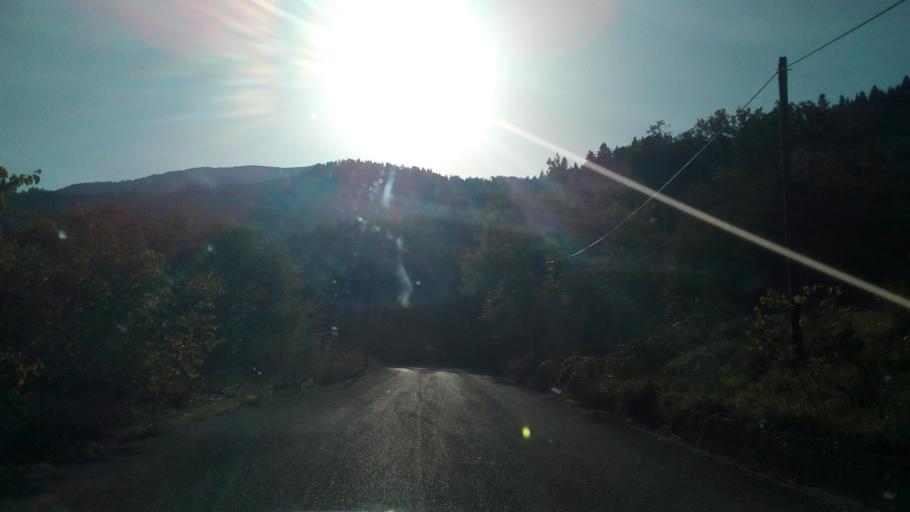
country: GR
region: West Greece
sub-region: Nomos Aitolias kai Akarnanias
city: Thermo
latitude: 38.6552
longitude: 21.8471
